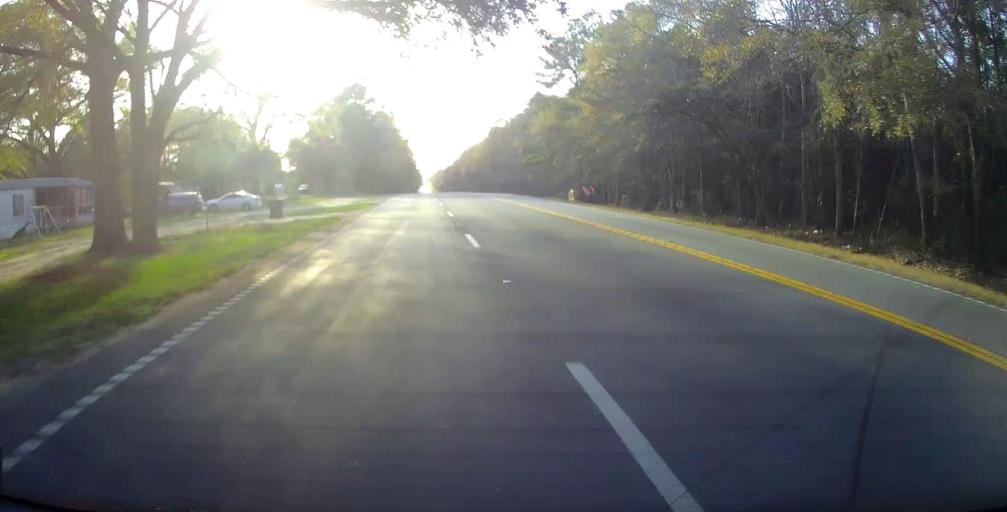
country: US
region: Georgia
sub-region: Evans County
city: Claxton
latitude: 32.1525
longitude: -81.8109
